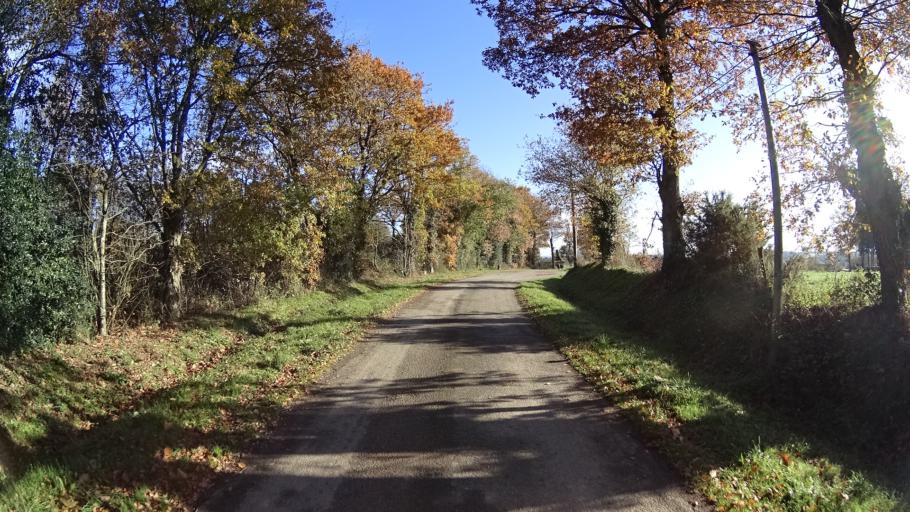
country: FR
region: Brittany
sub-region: Departement du Morbihan
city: Carentoir
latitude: 47.7942
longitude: -2.1986
